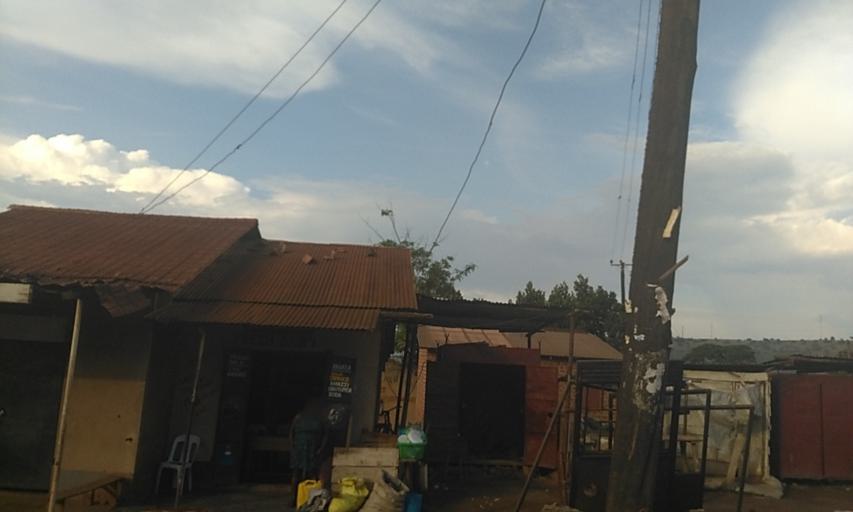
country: UG
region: Central Region
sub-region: Wakiso District
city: Kajansi
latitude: 0.2712
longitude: 32.5190
